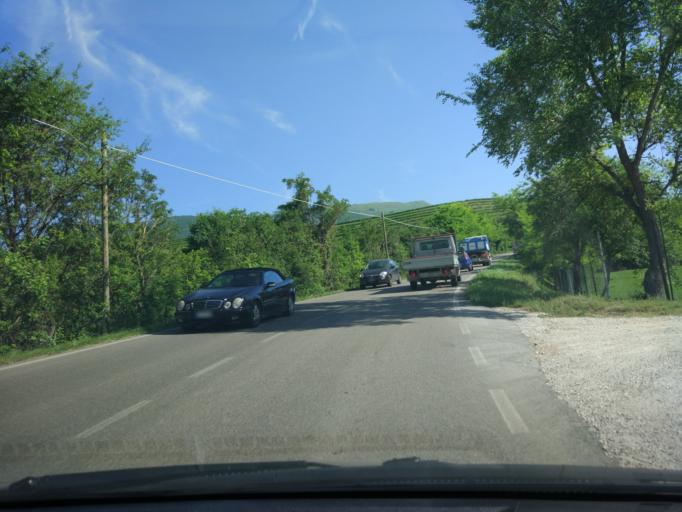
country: IT
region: Veneto
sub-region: Provincia di Verona
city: Rivoli Veronese
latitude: 45.5929
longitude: 10.8131
